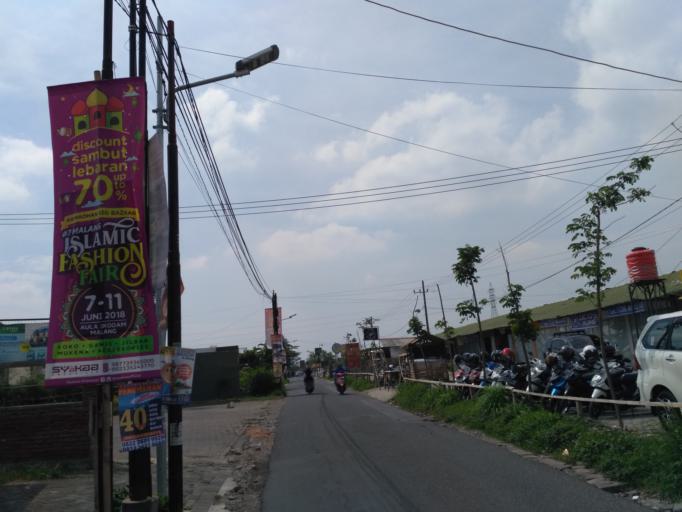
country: ID
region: East Java
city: Malang
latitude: -7.9345
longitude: 112.6290
